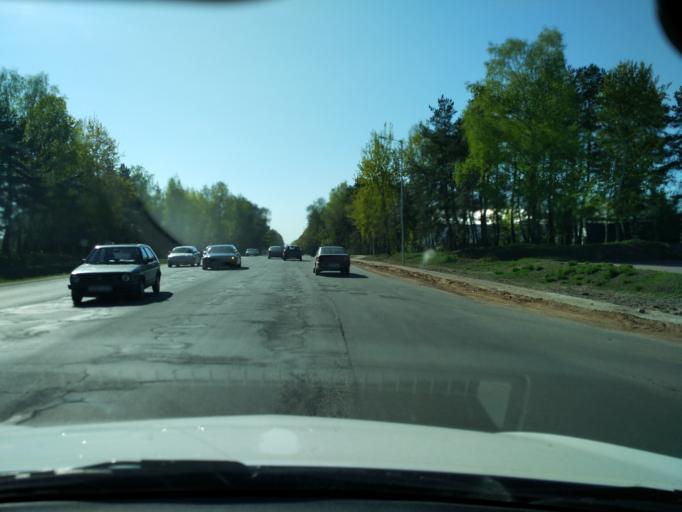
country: BY
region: Minsk
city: Borovlyany
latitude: 53.9652
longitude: 27.6648
